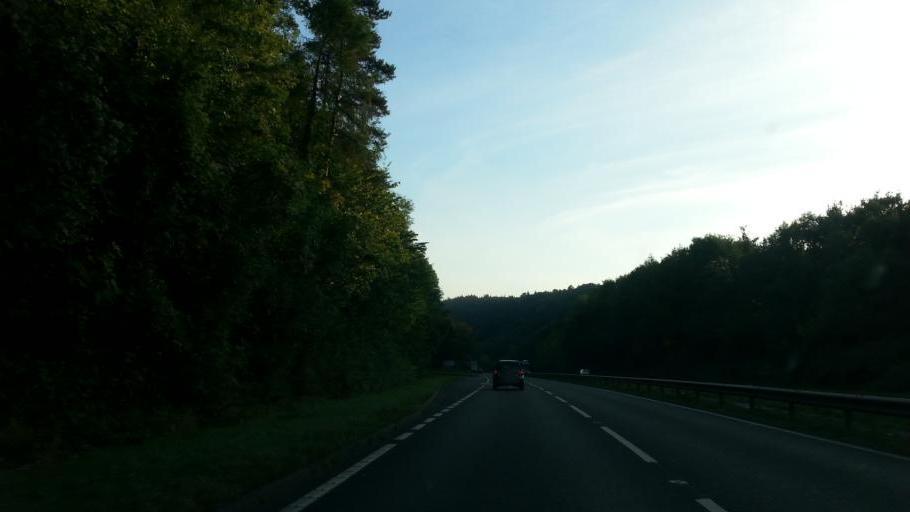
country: GB
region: England
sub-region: Herefordshire
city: Whitchurch
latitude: 51.8427
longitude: -2.6821
